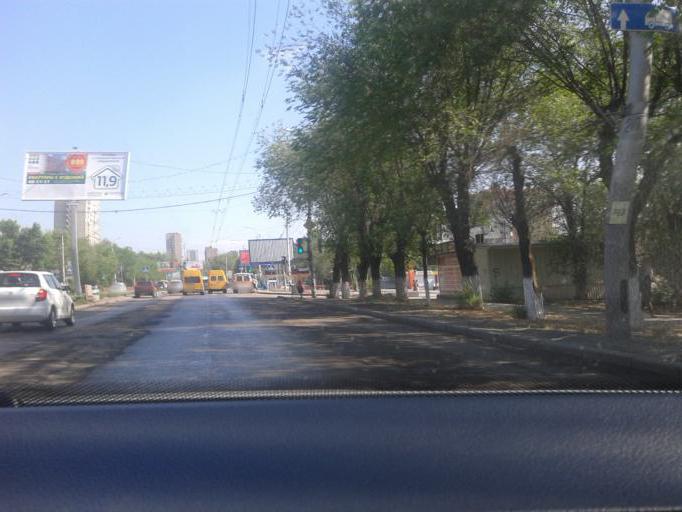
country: RU
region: Volgograd
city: Volgograd
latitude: 48.6117
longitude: 44.4226
